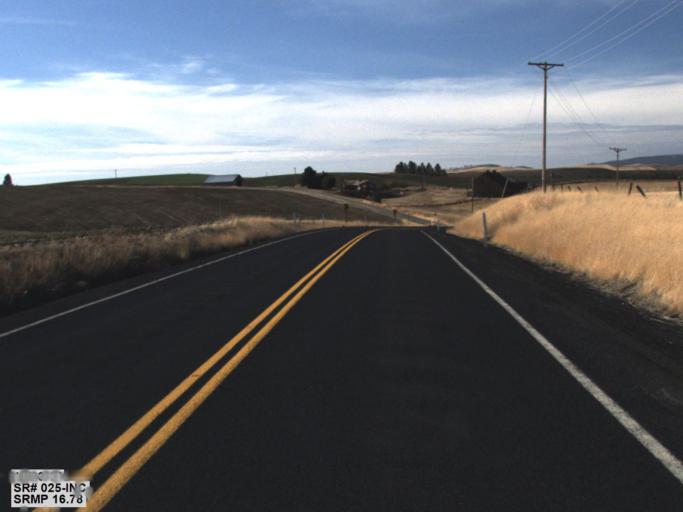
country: US
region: Washington
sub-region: Lincoln County
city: Davenport
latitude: 47.8609
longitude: -118.2406
